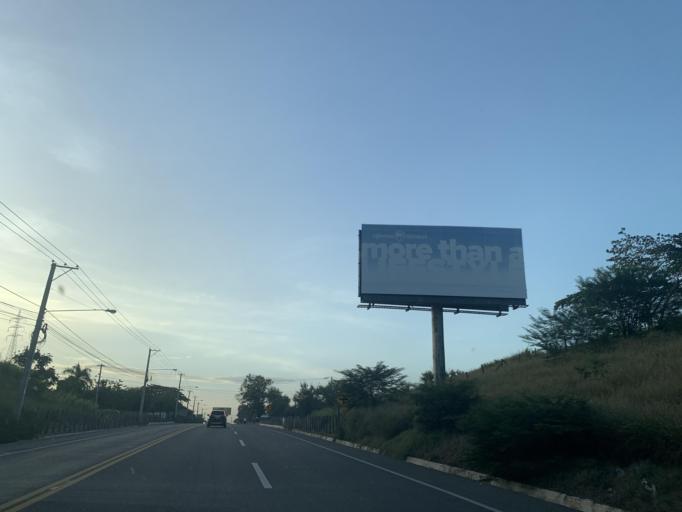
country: DO
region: Puerto Plata
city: Imbert
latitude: 19.7416
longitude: -70.8381
